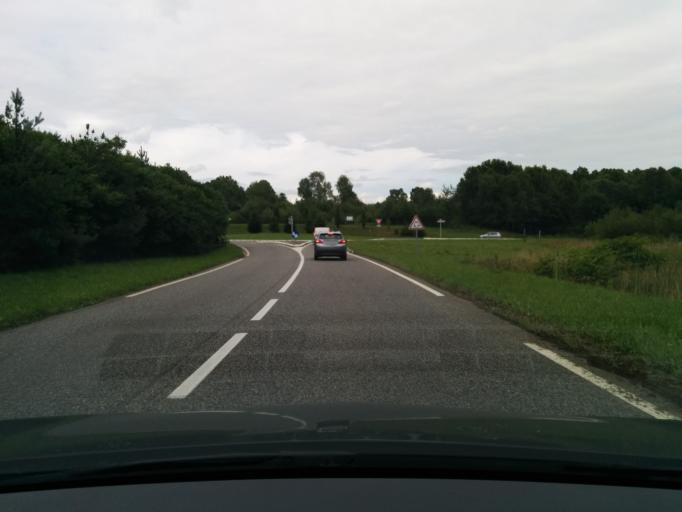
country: FR
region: Midi-Pyrenees
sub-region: Departement des Hautes-Pyrenees
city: La Barthe-de-Neste
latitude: 43.0795
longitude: 0.3629
